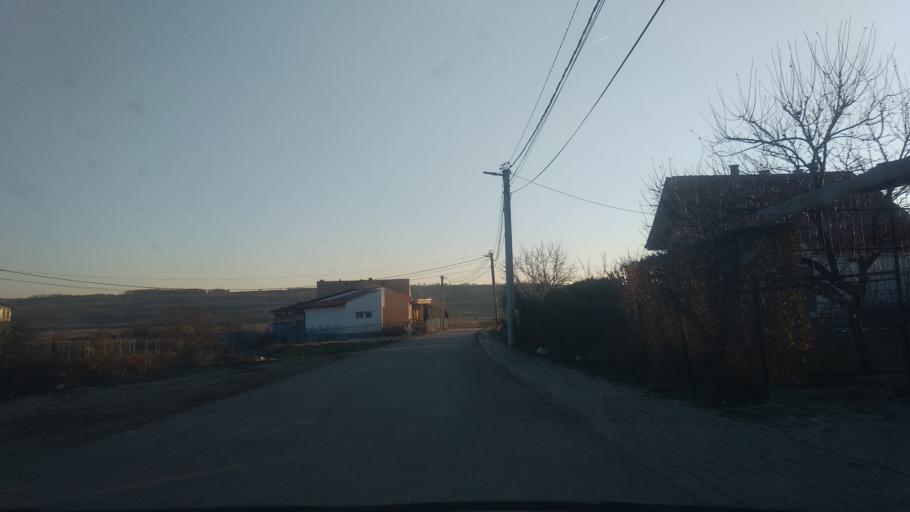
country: XK
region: Pristina
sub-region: Komuna e Prishtines
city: Pristina
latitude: 42.6025
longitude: 21.1825
